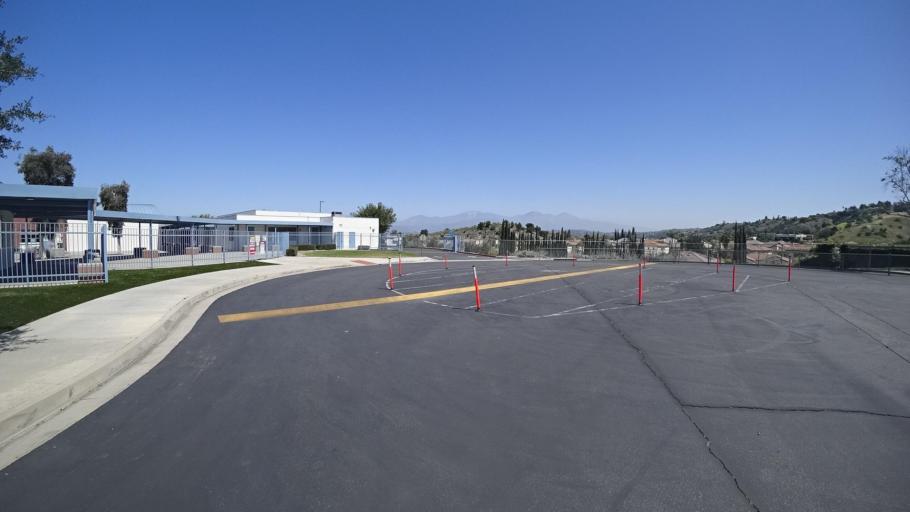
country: US
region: California
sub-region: Los Angeles County
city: Walnut
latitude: 33.9913
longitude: -117.8484
